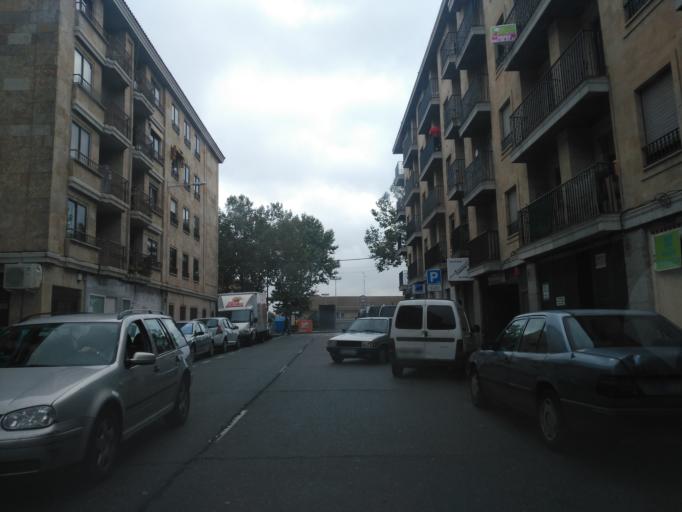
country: ES
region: Castille and Leon
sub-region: Provincia de Salamanca
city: Salamanca
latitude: 40.9581
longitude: -5.6659
